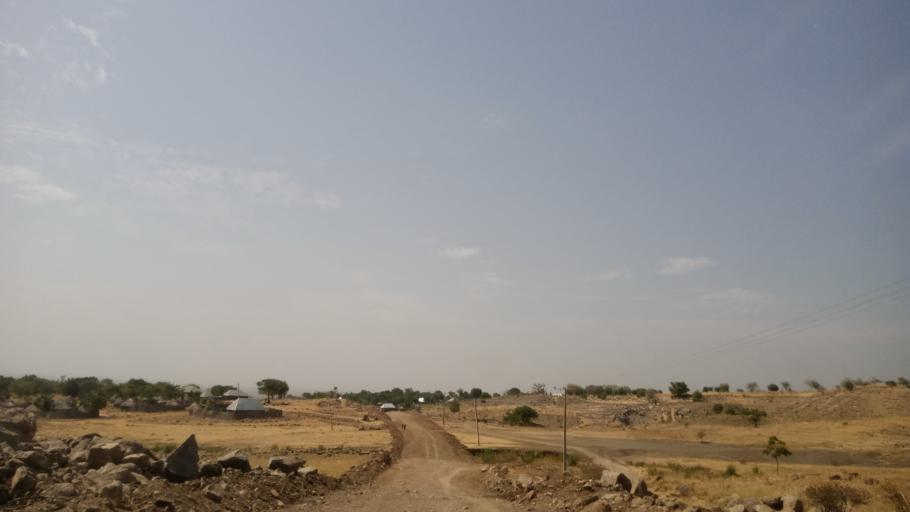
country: NG
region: Adamawa
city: Numan
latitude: 9.7002
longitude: 11.9227
